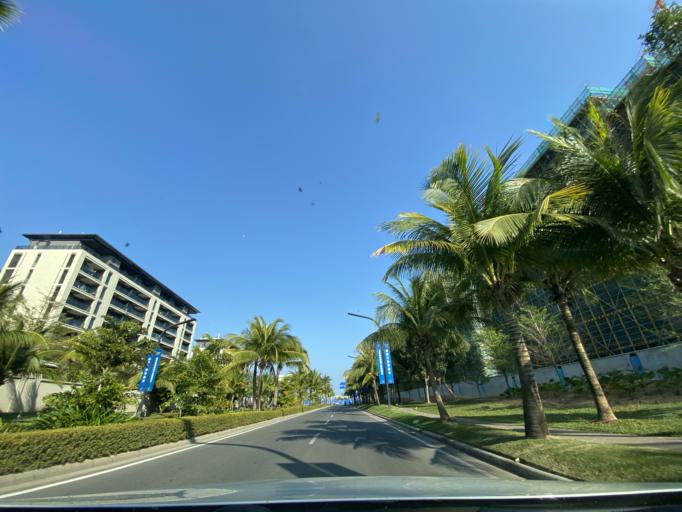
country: CN
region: Hainan
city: Xincun
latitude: 18.4236
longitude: 109.9591
